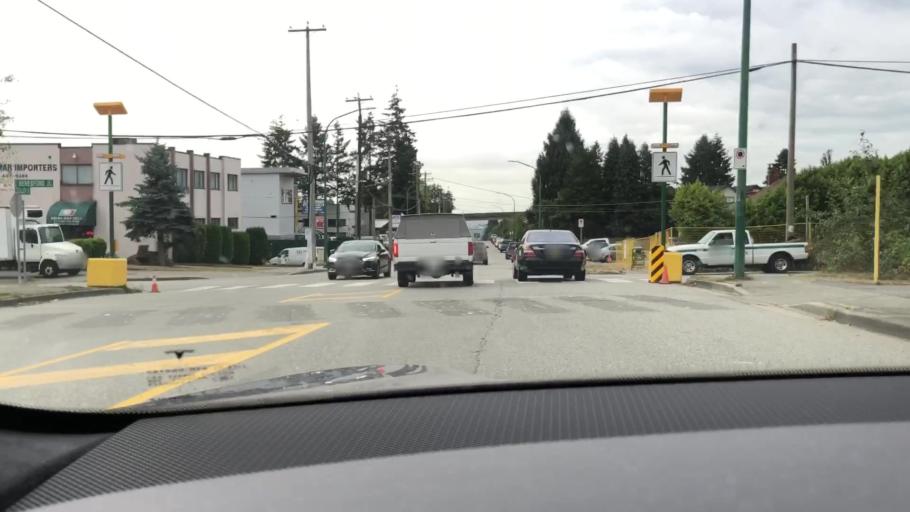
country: CA
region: British Columbia
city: Burnaby
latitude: 49.2174
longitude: -122.9721
